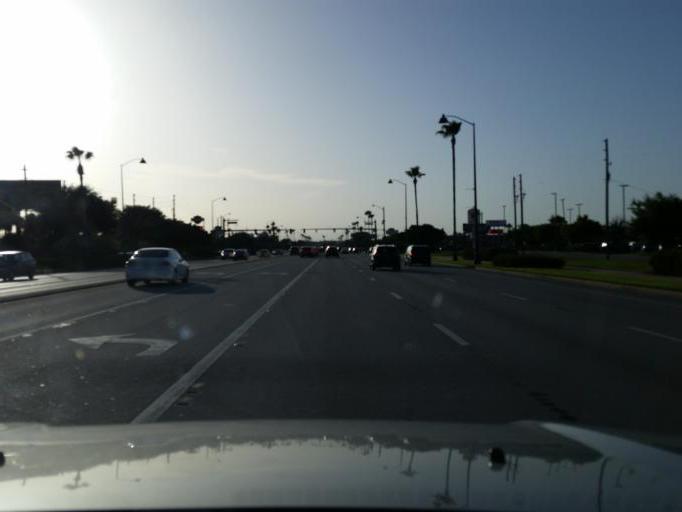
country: US
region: Florida
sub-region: Polk County
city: Citrus Ridge
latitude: 28.3390
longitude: -81.5954
